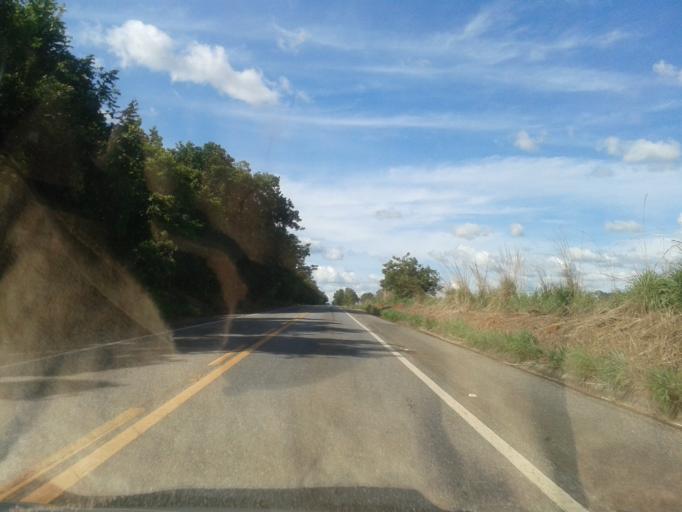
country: BR
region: Goias
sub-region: Mozarlandia
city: Mozarlandia
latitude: -14.9544
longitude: -50.5789
